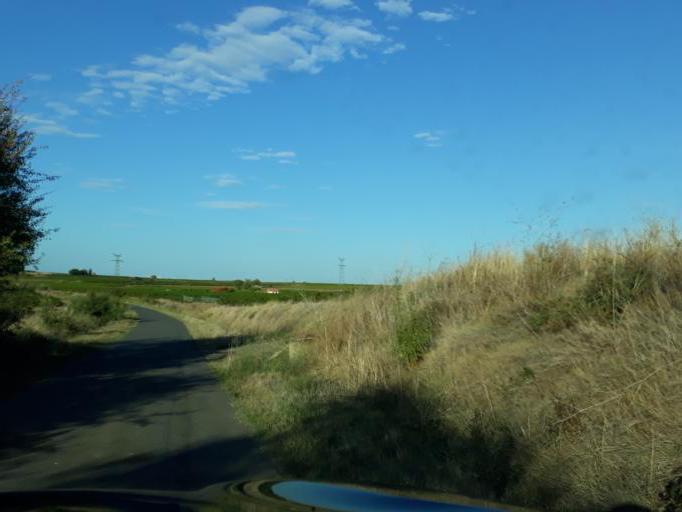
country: FR
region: Languedoc-Roussillon
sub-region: Departement de l'Herault
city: Florensac
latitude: 43.4053
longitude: 3.4740
